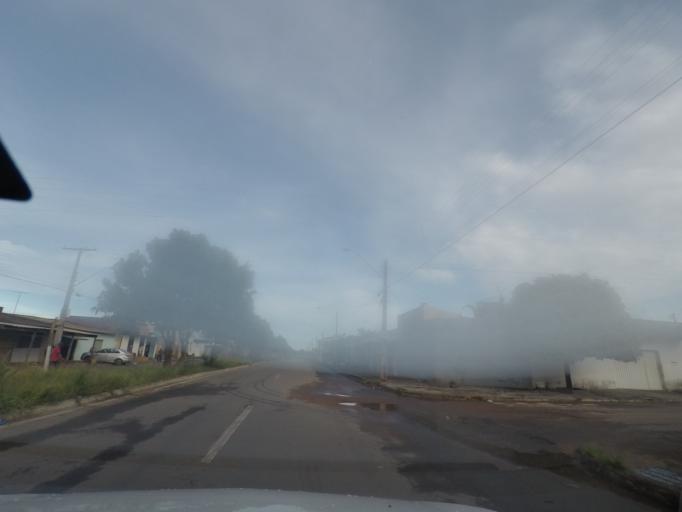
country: BR
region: Goias
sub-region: Aparecida De Goiania
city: Aparecida de Goiania
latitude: -16.7784
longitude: -49.3877
